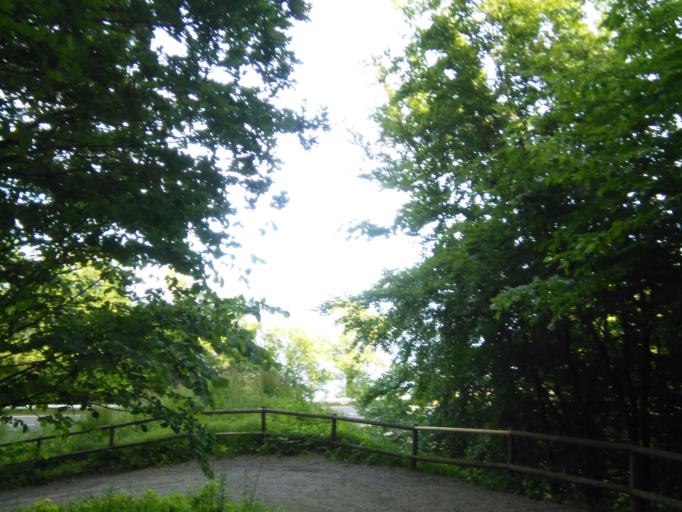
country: DK
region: Capital Region
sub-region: Bornholm Kommune
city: Akirkeby
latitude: 55.2274
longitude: 14.8833
